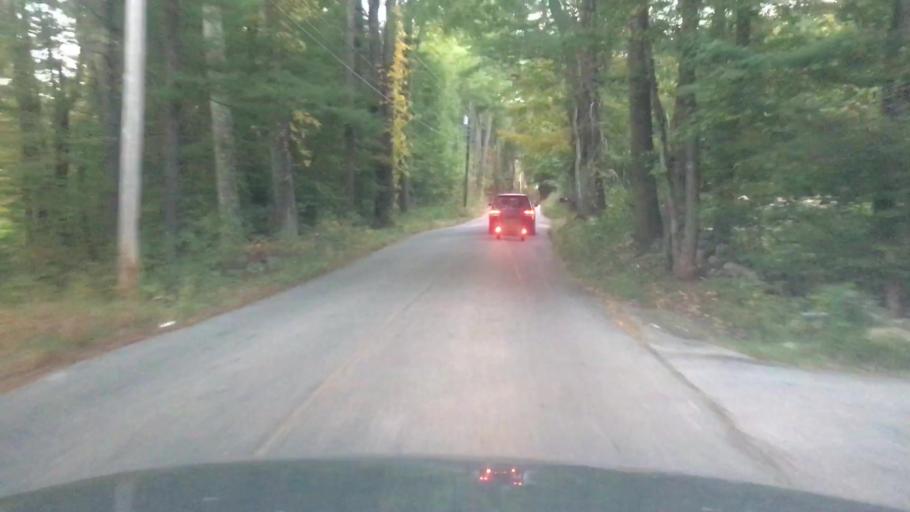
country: US
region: Massachusetts
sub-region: Worcester County
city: Charlton
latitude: 42.1216
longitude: -71.9817
